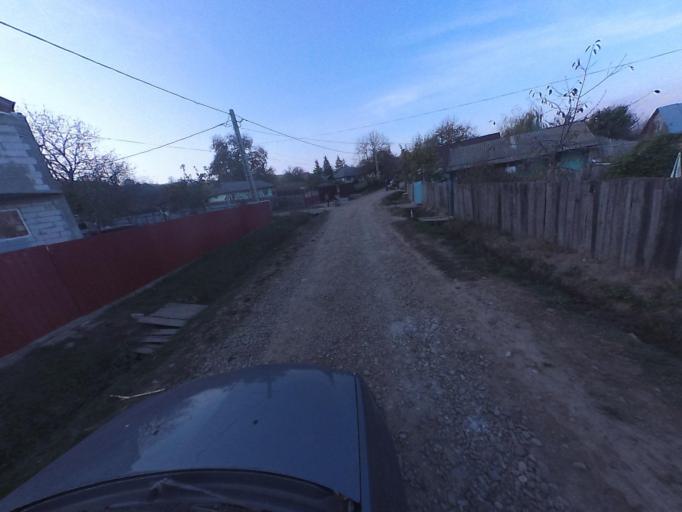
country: RO
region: Vaslui
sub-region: Comuna Bacesti
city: Bacesti
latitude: 46.8000
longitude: 27.2247
